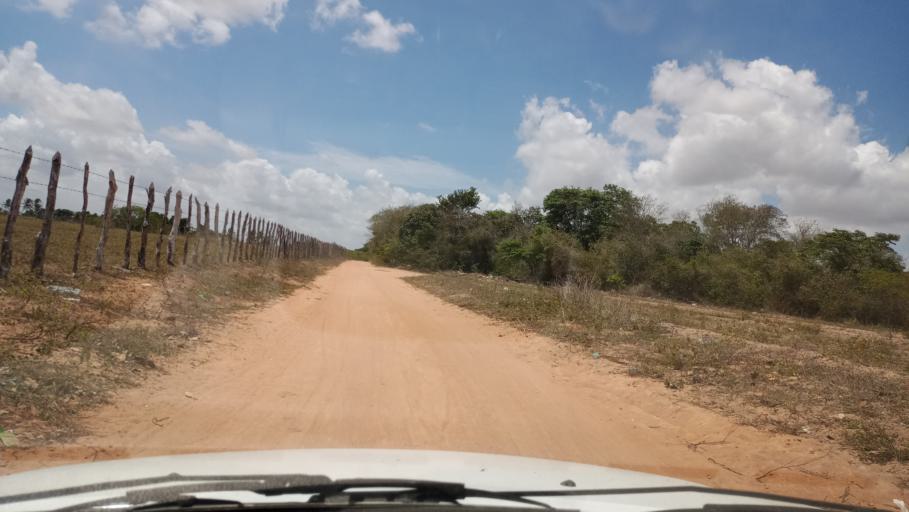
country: BR
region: Rio Grande do Norte
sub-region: Goianinha
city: Goianinha
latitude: -6.2829
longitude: -35.2847
